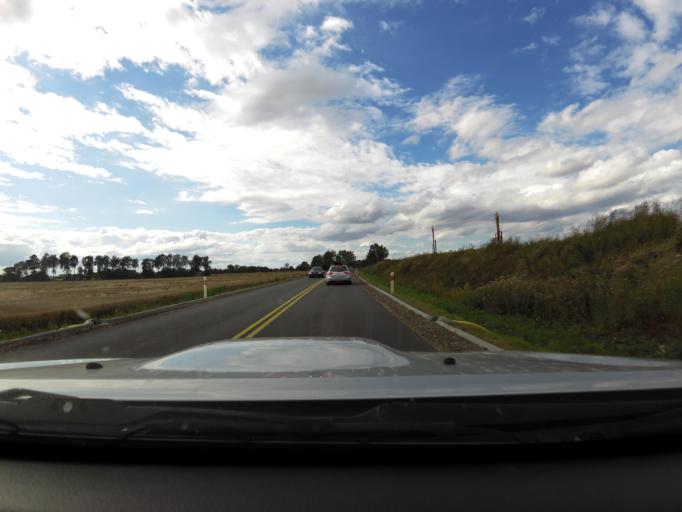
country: PL
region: Pomeranian Voivodeship
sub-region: Powiat gdanski
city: Cedry Wielkie
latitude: 54.2896
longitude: 18.8301
